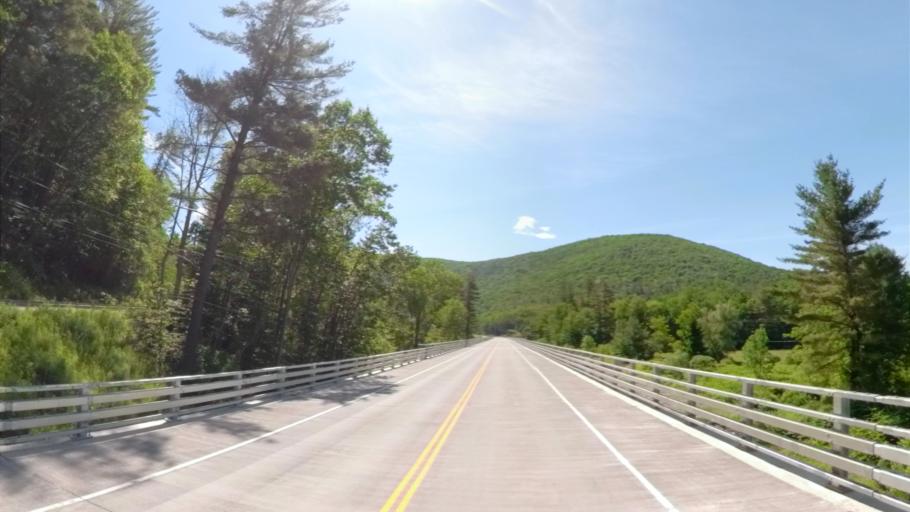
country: US
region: New York
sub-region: Ulster County
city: Shokan
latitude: 42.1058
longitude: -74.4485
